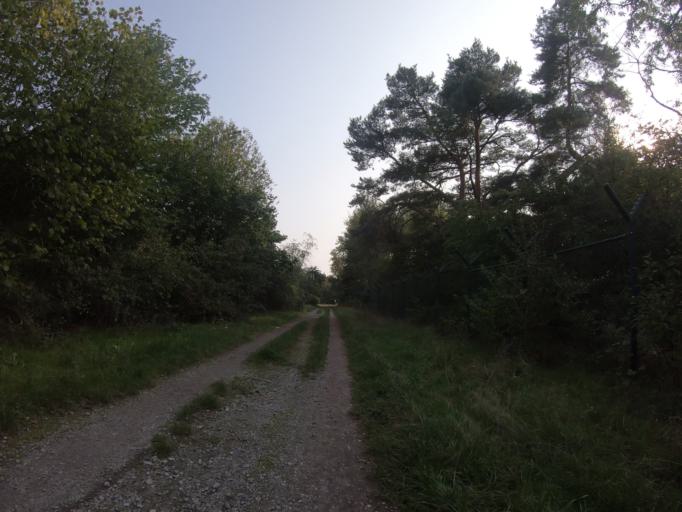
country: DE
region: Lower Saxony
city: Gifhorn
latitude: 52.4933
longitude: 10.5193
